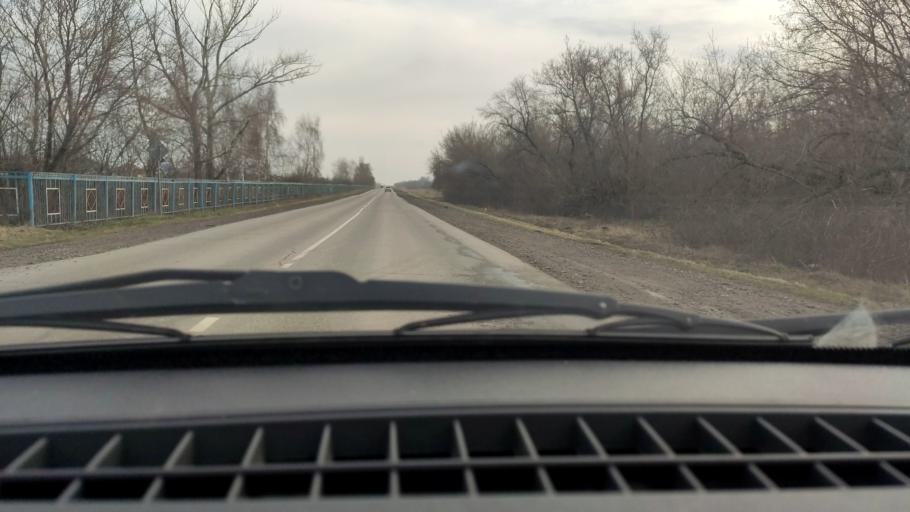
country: RU
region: Bashkortostan
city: Davlekanovo
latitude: 54.2954
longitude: 55.1261
